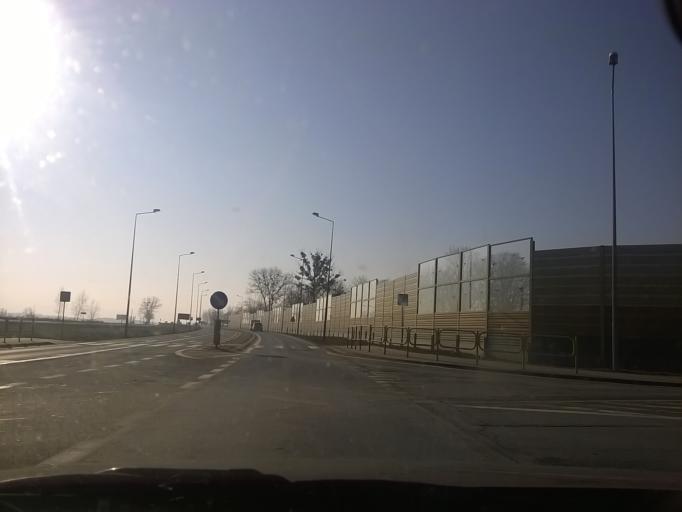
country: PL
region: Warmian-Masurian Voivodeship
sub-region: Powiat olsztynski
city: Barczewo
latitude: 53.8182
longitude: 20.6425
